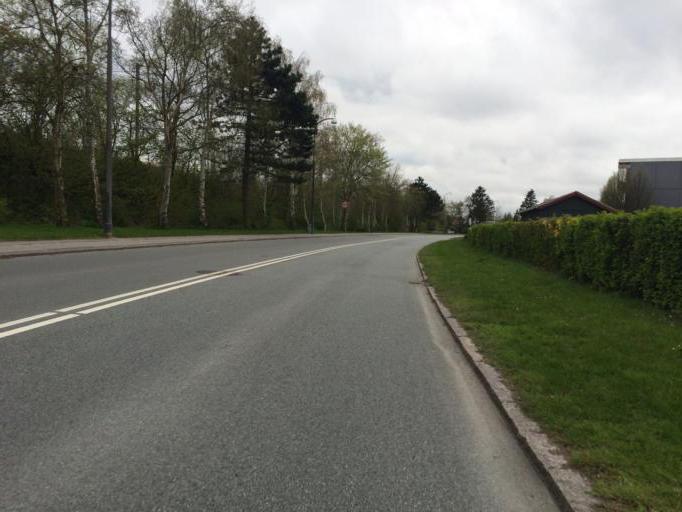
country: DK
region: Capital Region
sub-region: Vallensbaek Kommune
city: Vallensbaek
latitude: 55.6235
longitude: 12.3830
